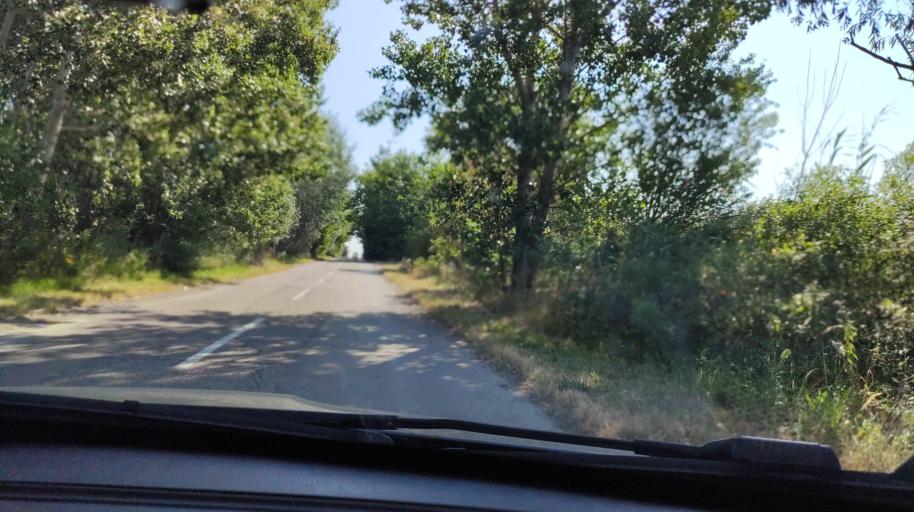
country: RS
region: Autonomna Pokrajina Vojvodina
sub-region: Severnobacki Okrug
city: Backa Topola
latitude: 45.8668
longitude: 19.6142
